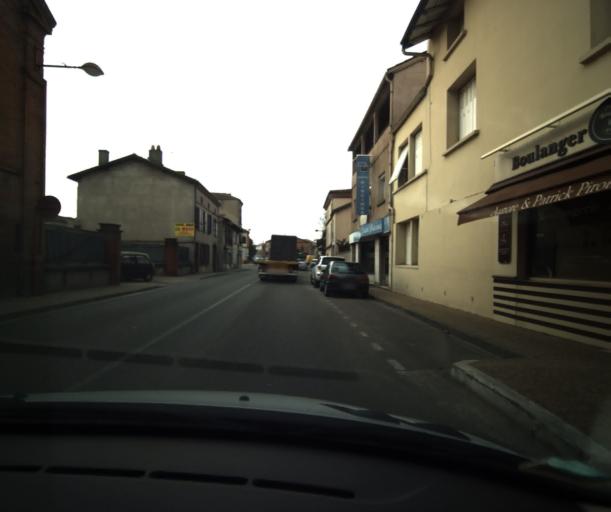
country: FR
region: Midi-Pyrenees
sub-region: Departement du Tarn-et-Garonne
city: Castelsarrasin
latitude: 44.0365
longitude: 1.1119
